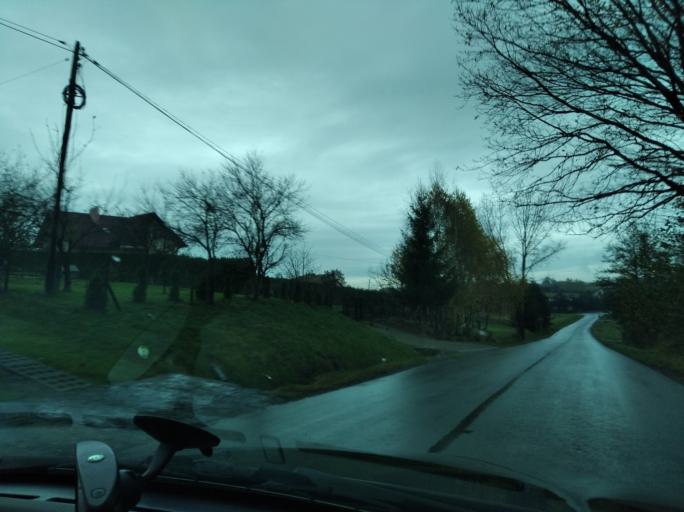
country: PL
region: Subcarpathian Voivodeship
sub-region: Powiat rzeszowski
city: Tyczyn
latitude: 49.9247
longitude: 22.0278
